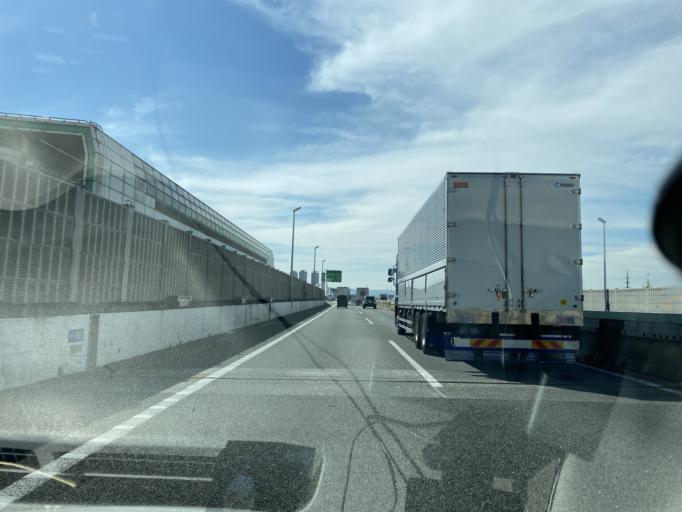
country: JP
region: Osaka
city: Kadoma
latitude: 34.7659
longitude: 135.5679
